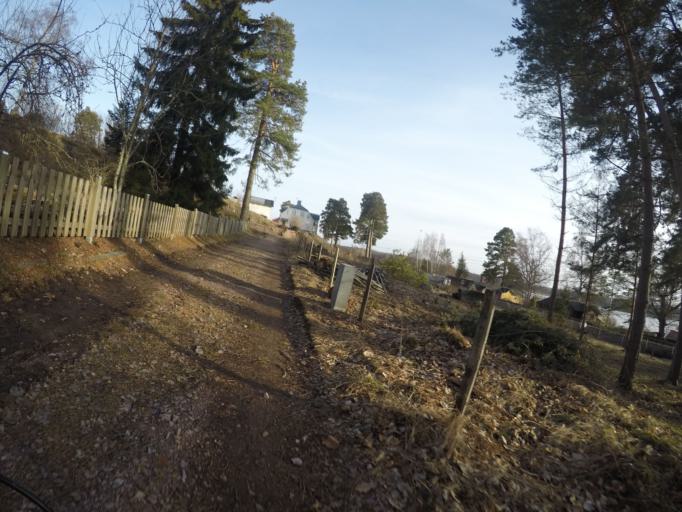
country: SE
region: Soedermanland
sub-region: Eskilstuna Kommun
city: Kvicksund
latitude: 59.4565
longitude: 16.3153
